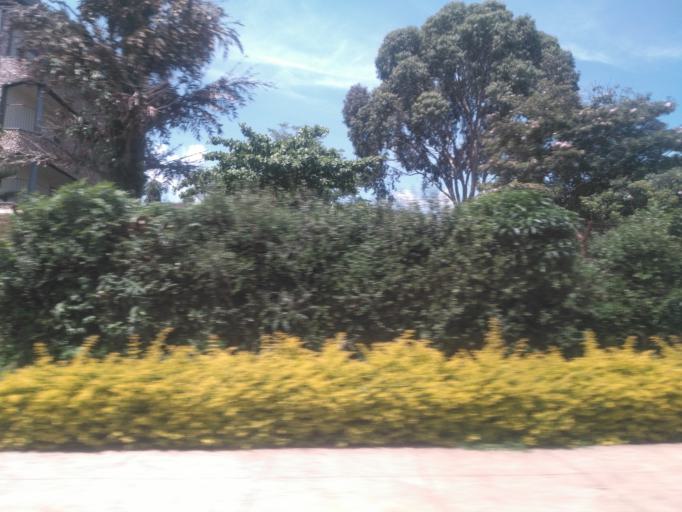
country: UG
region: Central Region
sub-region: Wakiso District
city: Entebbe
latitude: 0.0445
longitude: 32.4638
